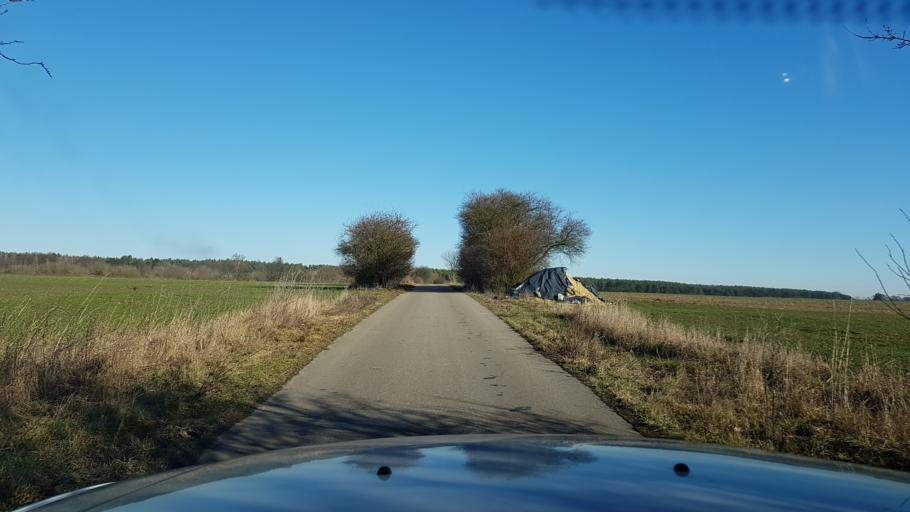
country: PL
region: West Pomeranian Voivodeship
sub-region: Powiat pyrzycki
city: Przelewice
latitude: 53.0471
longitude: 15.0522
